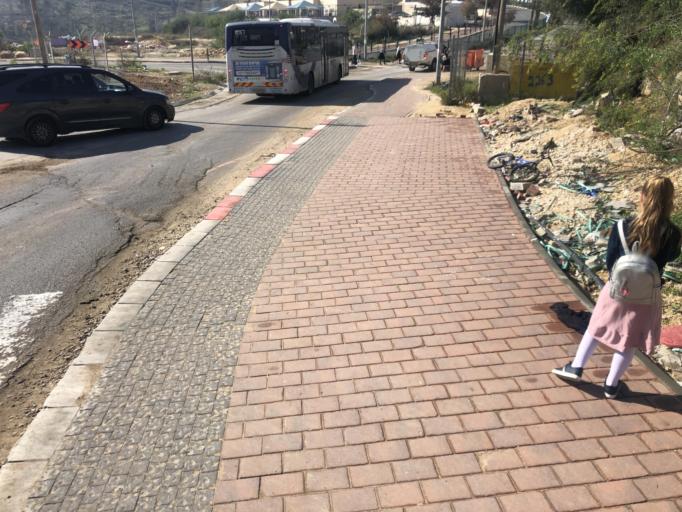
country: IL
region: Jerusalem
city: Modiin Ilit
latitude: 31.9250
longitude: 35.0460
